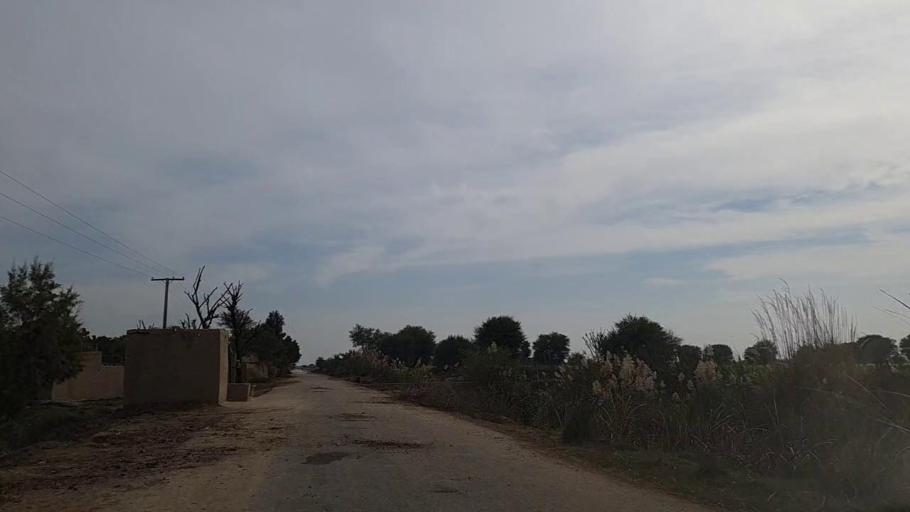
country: PK
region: Sindh
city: Daur
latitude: 26.4166
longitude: 68.4884
